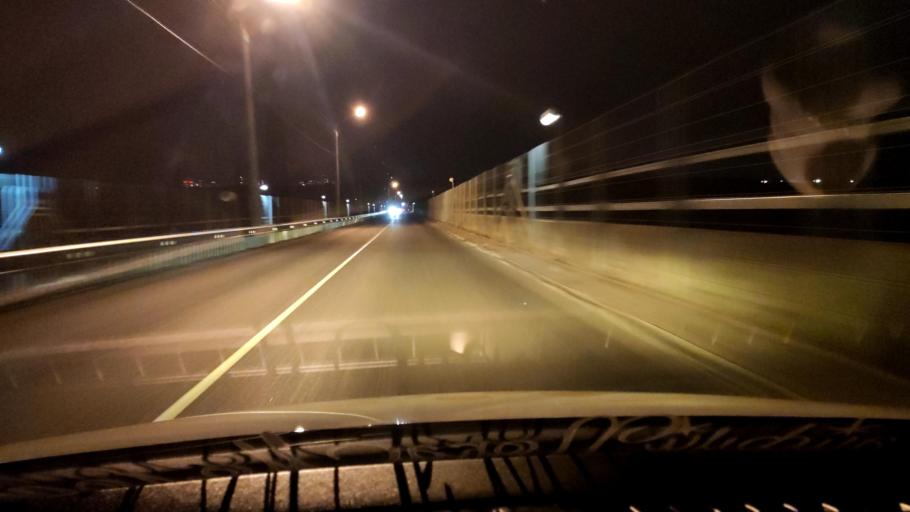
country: RU
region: Voronezj
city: Shilovo
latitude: 51.5429
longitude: 39.1372
